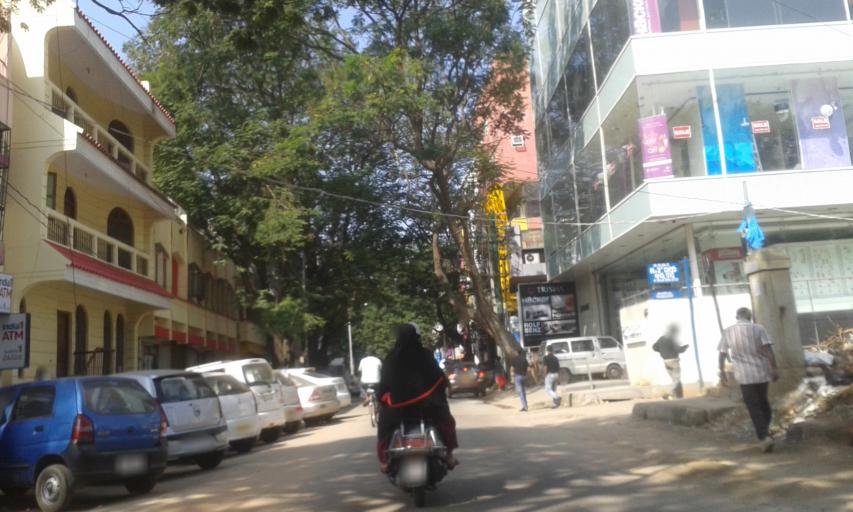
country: IN
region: Karnataka
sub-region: Bangalore Urban
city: Bangalore
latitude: 12.9676
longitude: 77.6079
